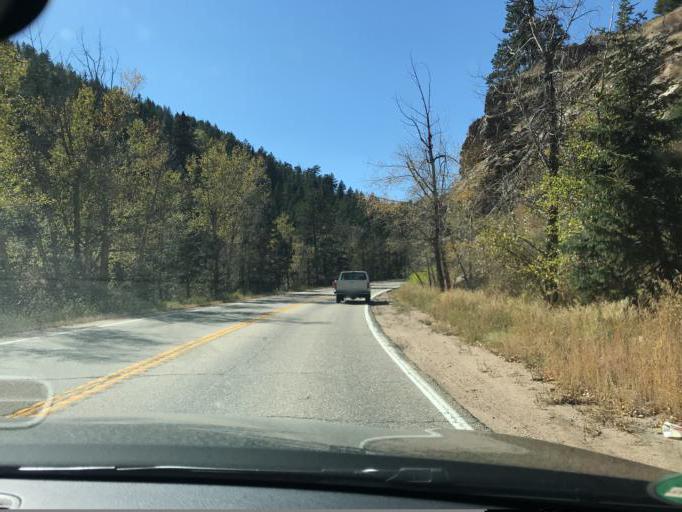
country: US
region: Colorado
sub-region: Boulder County
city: Nederland
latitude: 39.9826
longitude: -105.4468
